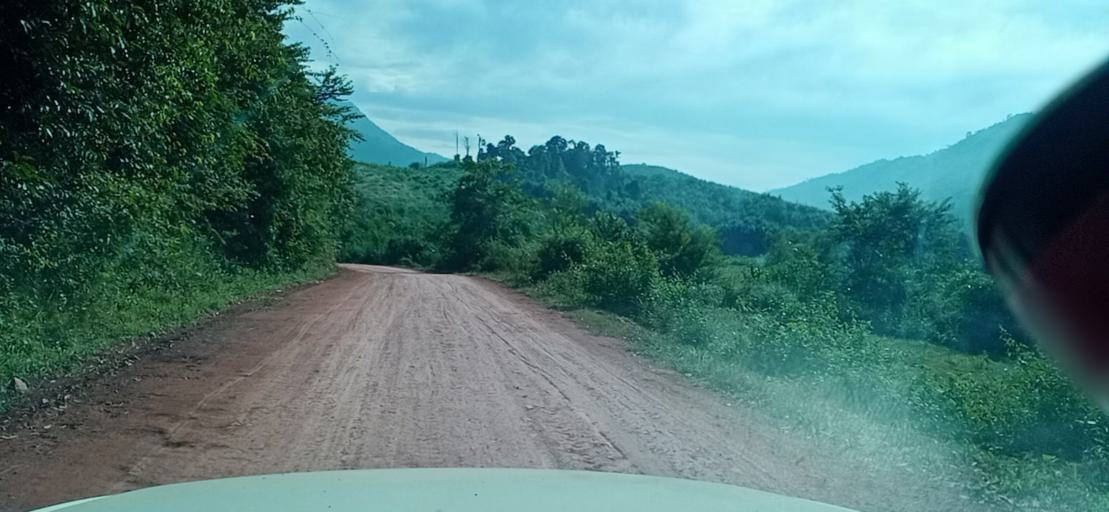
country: TH
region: Changwat Bueng Kan
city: Pak Khat
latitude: 18.6697
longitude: 103.1984
